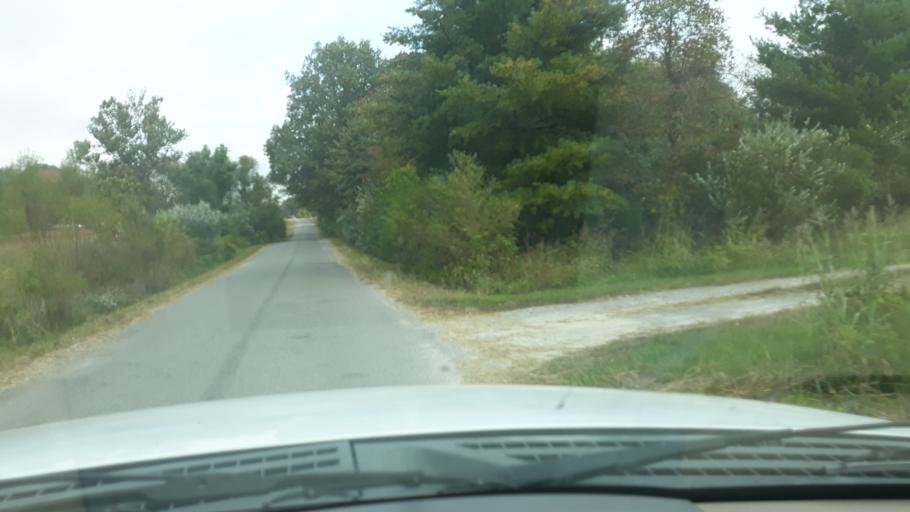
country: US
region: Illinois
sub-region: Saline County
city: Eldorado
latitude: 37.8311
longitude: -88.4849
